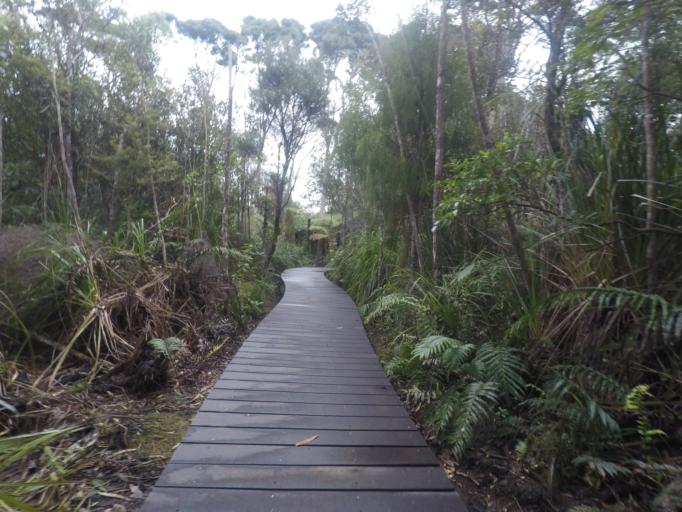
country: NZ
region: Auckland
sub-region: Auckland
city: Titirangi
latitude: -37.0019
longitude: 174.5390
